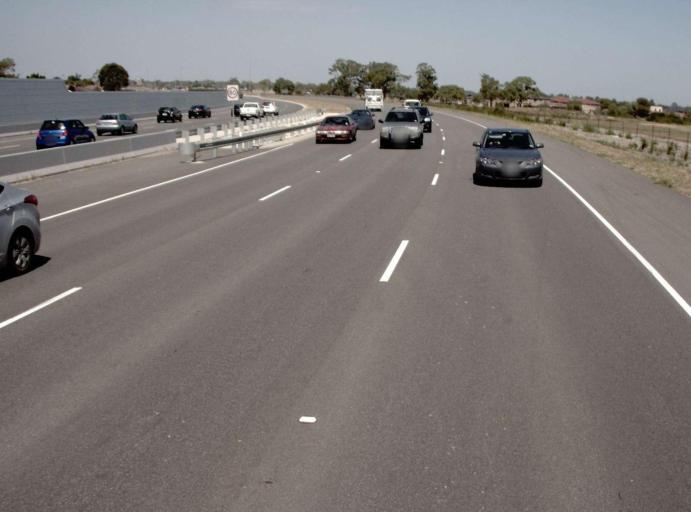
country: AU
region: Victoria
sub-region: Greater Dandenong
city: Keysborough
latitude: -37.9954
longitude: 145.1575
